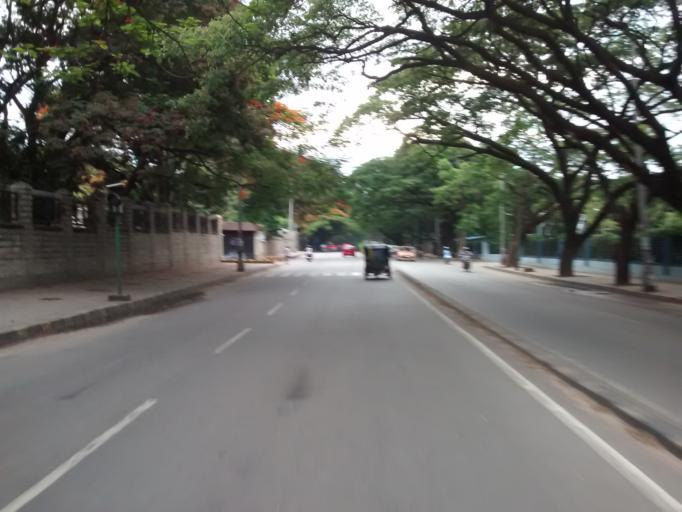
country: IN
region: Karnataka
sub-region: Bangalore Urban
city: Bangalore
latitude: 12.9580
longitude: 77.6693
